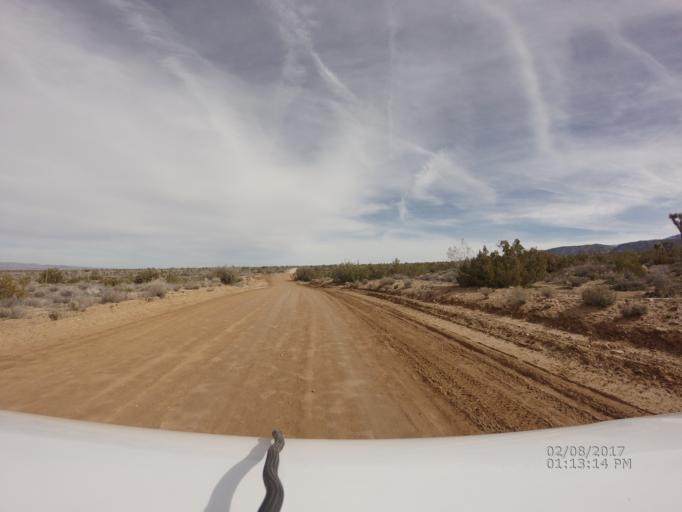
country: US
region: California
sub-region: Los Angeles County
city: Lake Los Angeles
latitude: 34.4748
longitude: -117.7863
